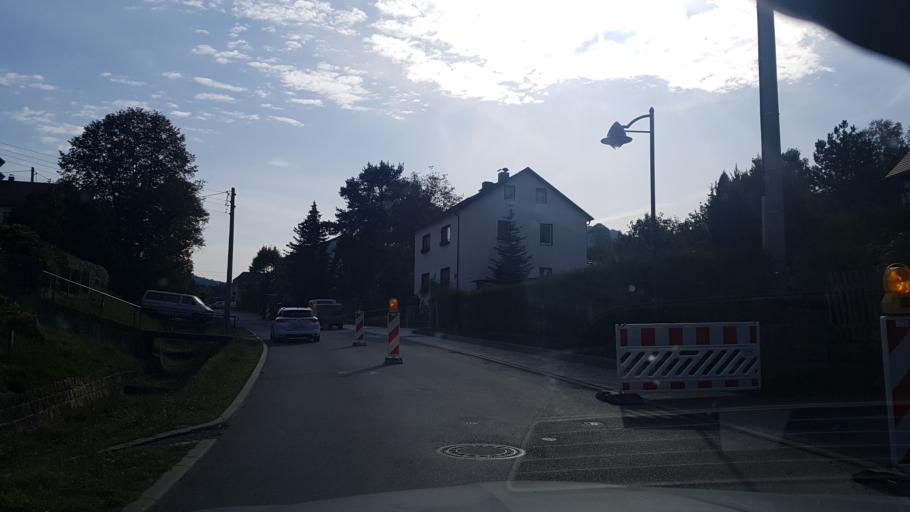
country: DE
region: Saxony
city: Konigstein
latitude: 50.9112
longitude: 14.0749
